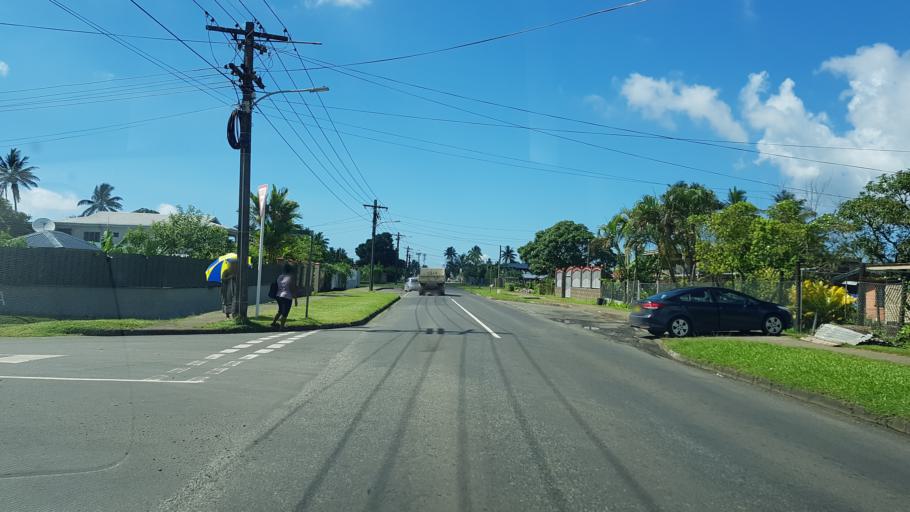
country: FJ
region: Central
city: Suva
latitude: -18.1315
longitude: 178.4592
